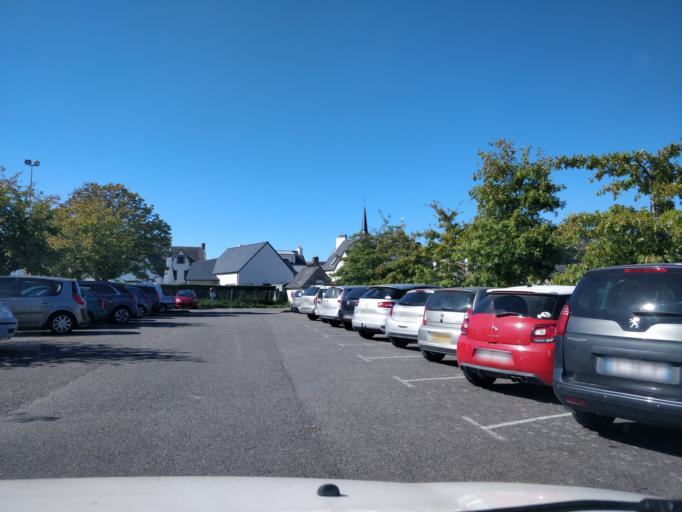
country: FR
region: Brittany
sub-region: Departement du Morbihan
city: Locmariaquer
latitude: 47.5678
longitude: -2.9430
